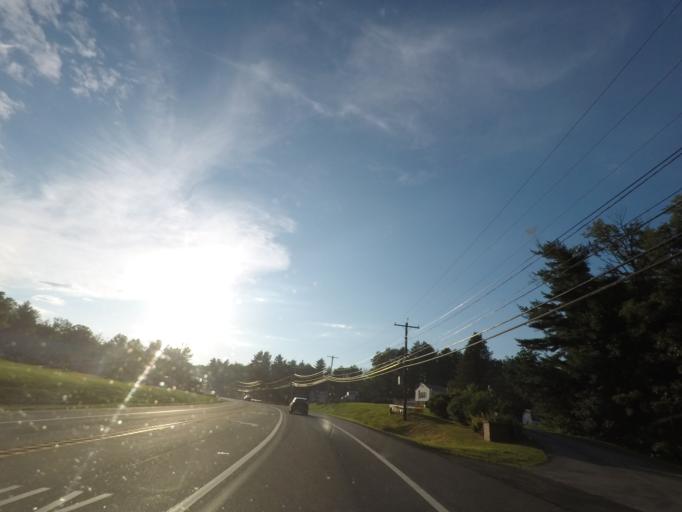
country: US
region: Massachusetts
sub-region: Worcester County
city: Fiskdale
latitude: 42.1125
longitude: -72.1502
